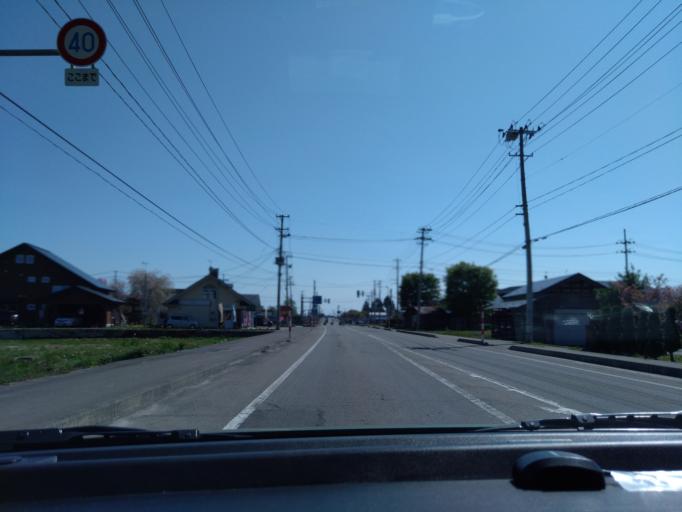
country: JP
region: Akita
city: Kakunodatemachi
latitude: 39.5852
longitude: 140.5708
